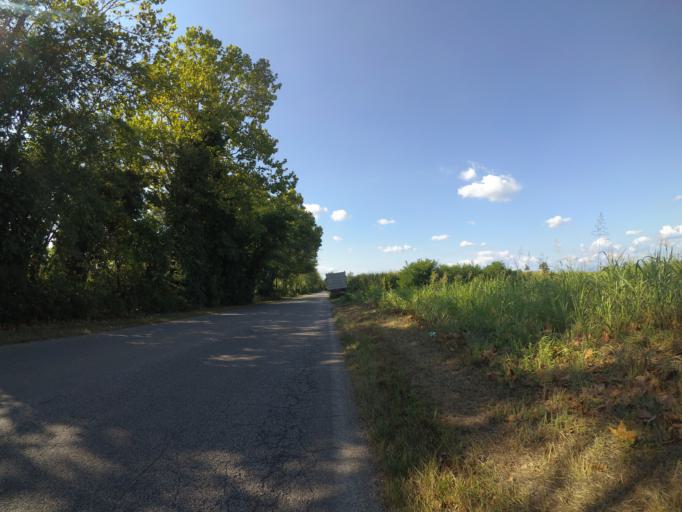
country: IT
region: Friuli Venezia Giulia
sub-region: Provincia di Udine
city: Mortegliano
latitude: 45.9578
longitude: 13.1677
